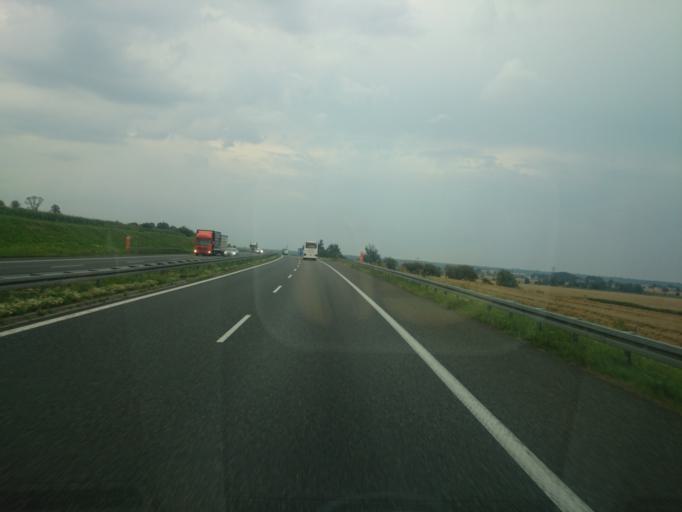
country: PL
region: Silesian Voivodeship
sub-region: Powiat gliwicki
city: Rudziniec
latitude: 50.4029
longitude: 18.4225
